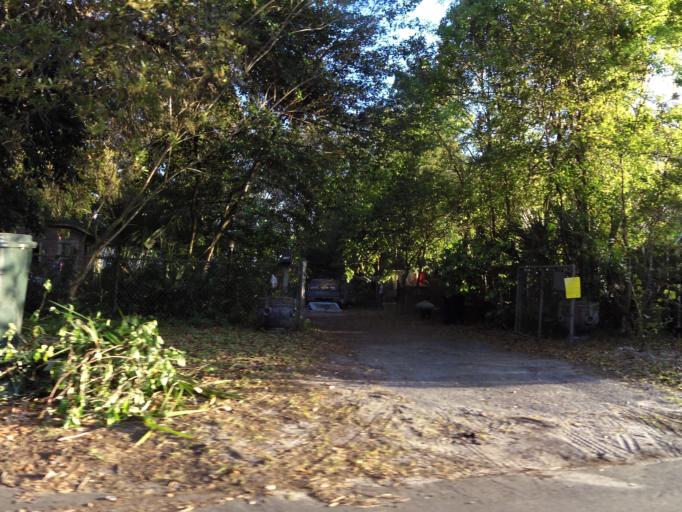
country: US
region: Florida
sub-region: Duval County
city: Jacksonville
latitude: 30.2856
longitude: -81.6483
